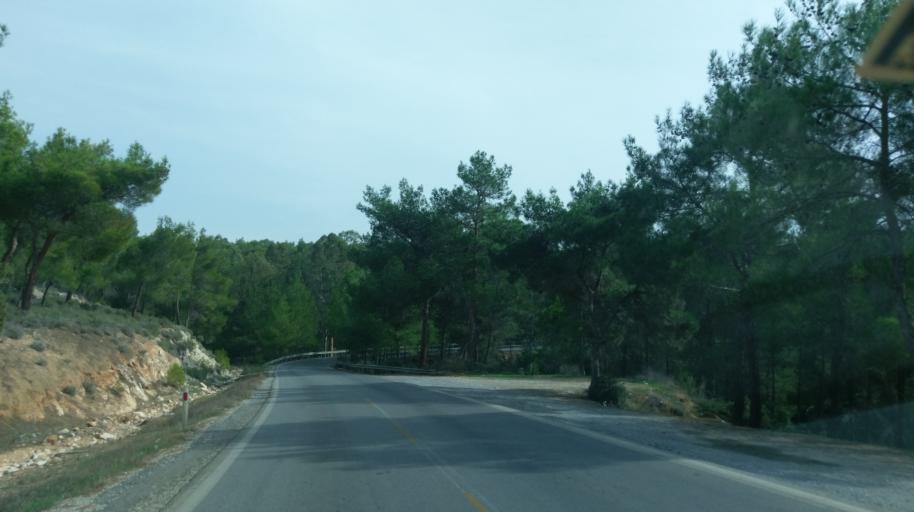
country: CY
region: Lefkosia
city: Morfou
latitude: 35.2705
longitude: 33.0429
